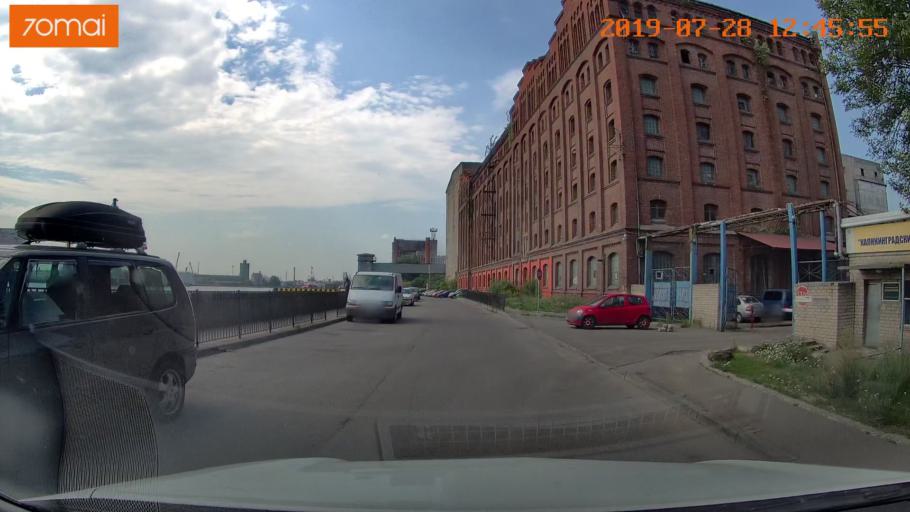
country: RU
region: Kaliningrad
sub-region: Gorod Kaliningrad
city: Kaliningrad
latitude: 54.7074
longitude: 20.4586
